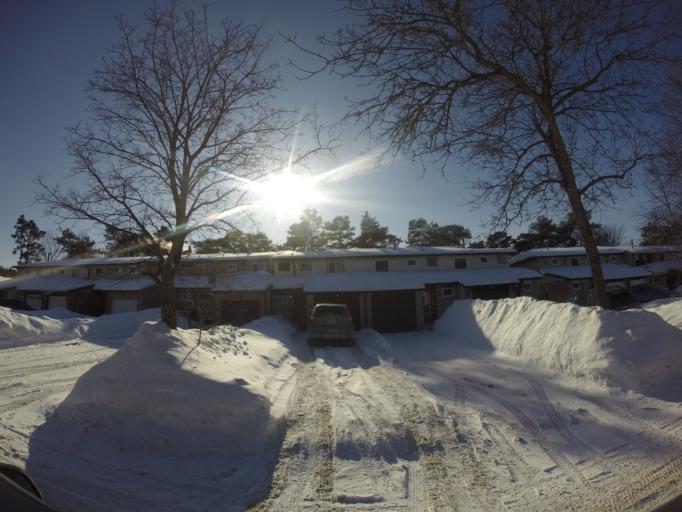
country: CA
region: Ontario
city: Barrie
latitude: 44.3966
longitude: -79.7188
